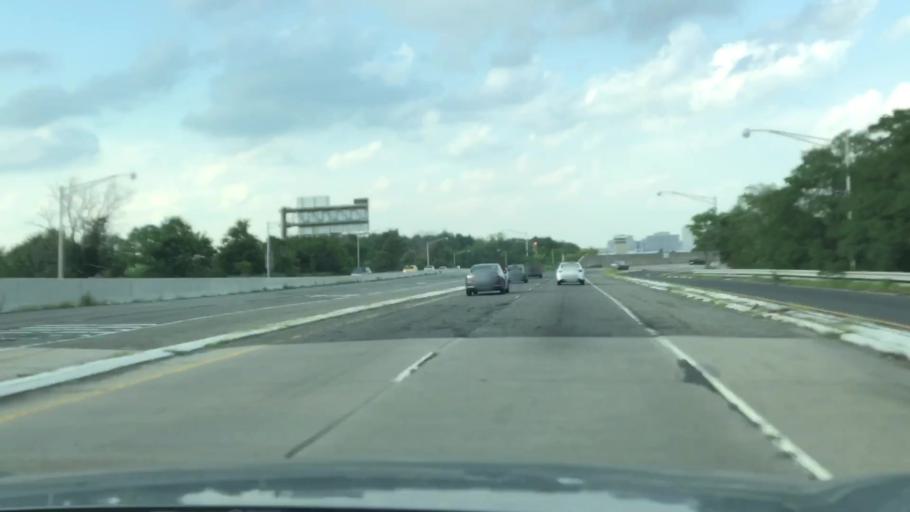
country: US
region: New Jersey
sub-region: Essex County
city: Newark
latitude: 40.7088
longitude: -74.1775
